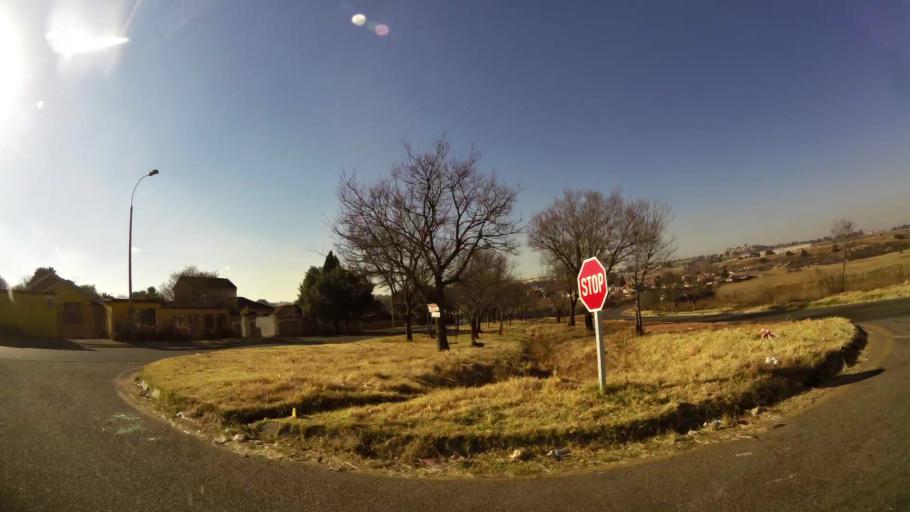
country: ZA
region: Gauteng
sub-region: City of Johannesburg Metropolitan Municipality
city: Roodepoort
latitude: -26.1529
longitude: 27.8420
